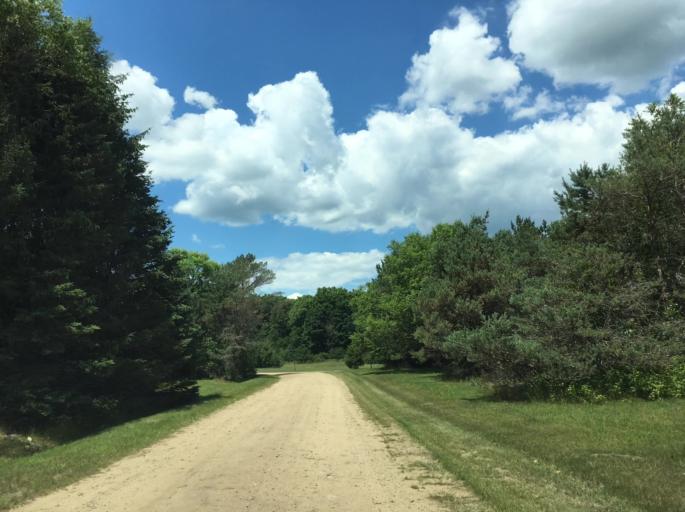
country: US
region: Michigan
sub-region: Osceola County
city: Evart
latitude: 43.8600
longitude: -85.3758
